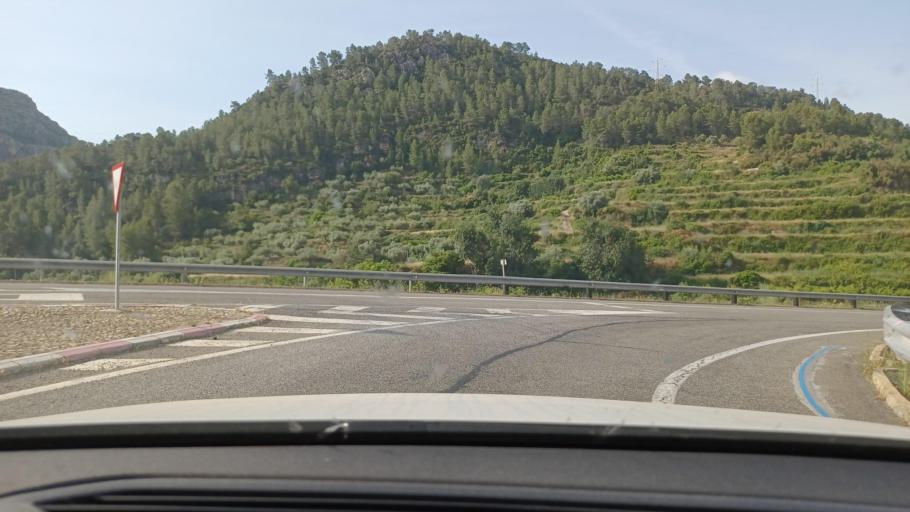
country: ES
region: Catalonia
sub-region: Provincia de Tarragona
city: Benifallet
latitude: 40.9805
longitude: 0.5249
